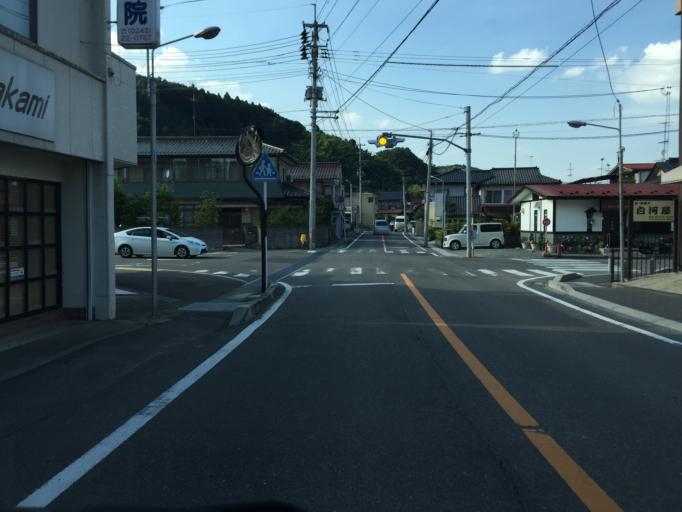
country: JP
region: Fukushima
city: Nihommatsu
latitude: 37.5624
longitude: 140.4119
